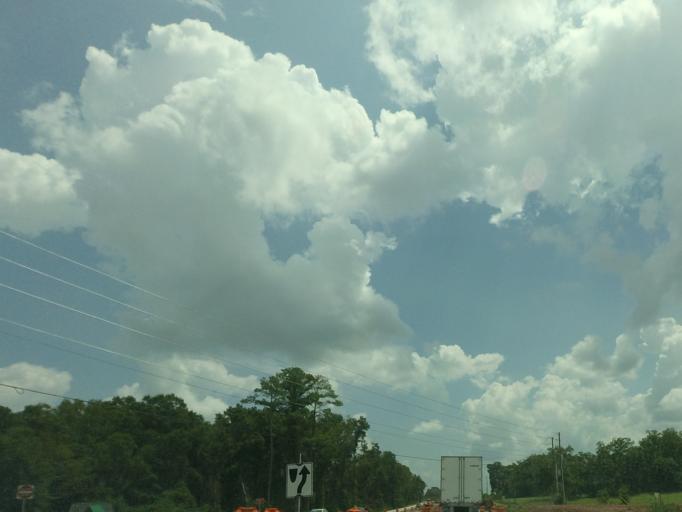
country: US
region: Georgia
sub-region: Houston County
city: Centerville
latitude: 32.5544
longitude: -83.6848
